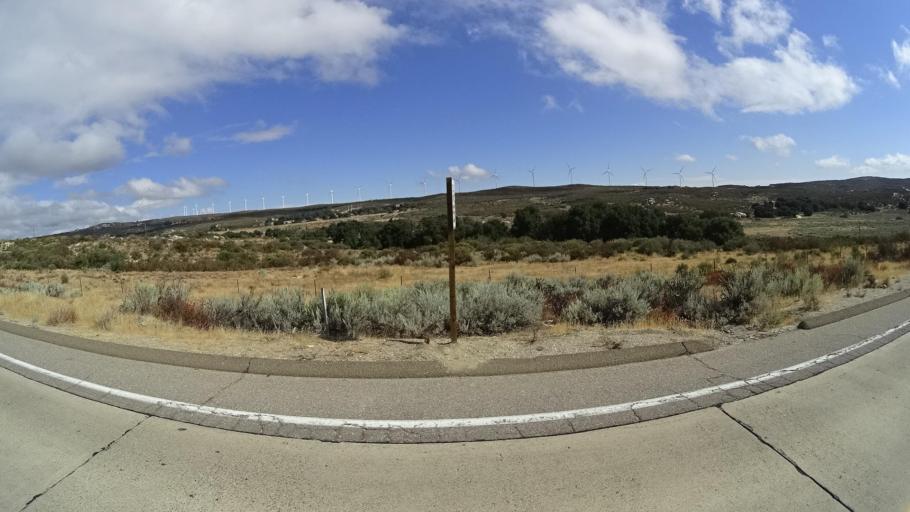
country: US
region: California
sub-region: San Diego County
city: Campo
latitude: 32.6960
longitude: -116.3468
